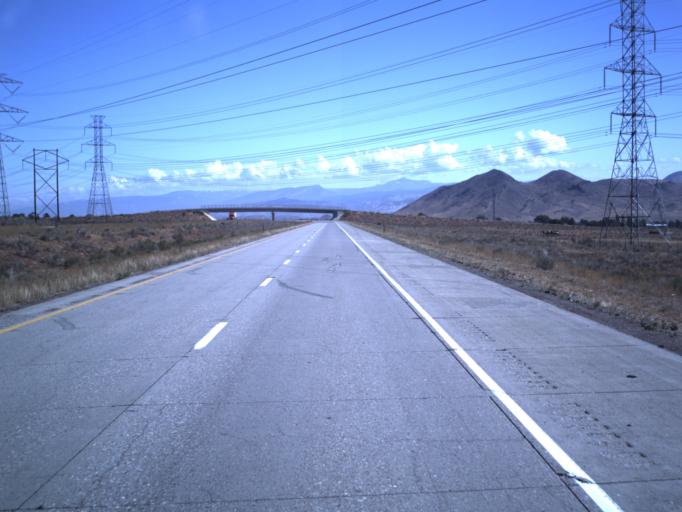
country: US
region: Utah
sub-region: Sevier County
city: Aurora
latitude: 38.8569
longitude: -111.9901
